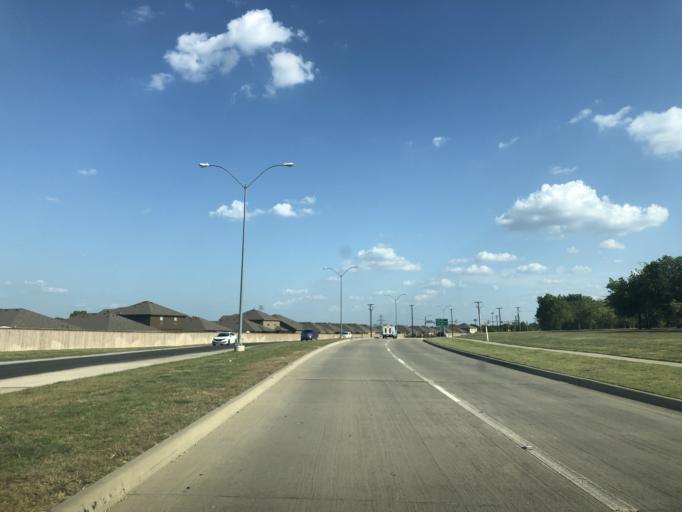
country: US
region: Texas
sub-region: Tarrant County
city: Saginaw
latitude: 32.8381
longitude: -97.3852
